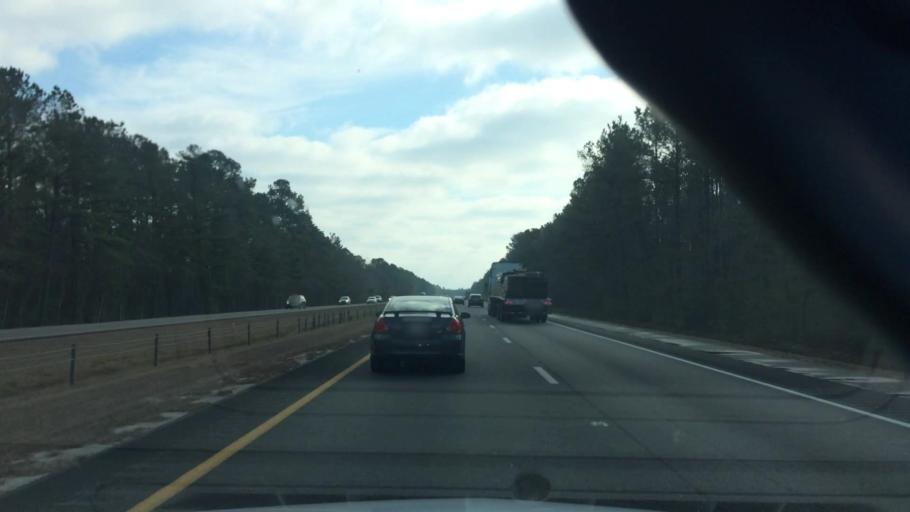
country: US
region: North Carolina
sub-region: Pender County
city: Burgaw
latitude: 34.6029
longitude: -77.9142
